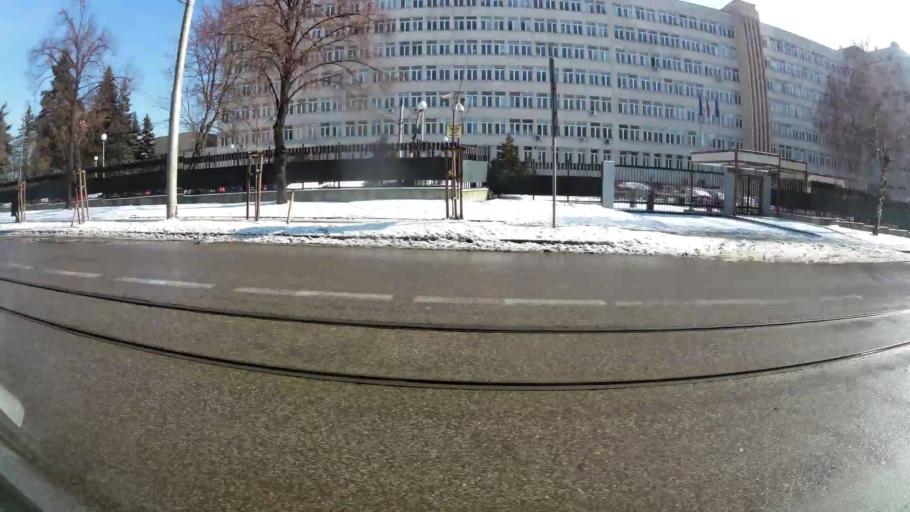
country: BG
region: Sofia-Capital
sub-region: Stolichna Obshtina
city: Sofia
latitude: 42.6637
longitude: 23.3174
